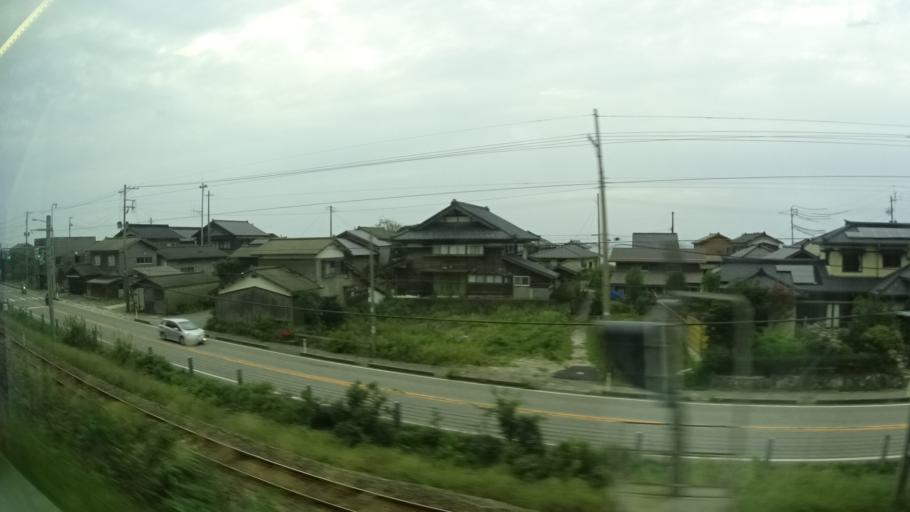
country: JP
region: Niigata
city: Murakami
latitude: 38.5389
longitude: 139.5496
